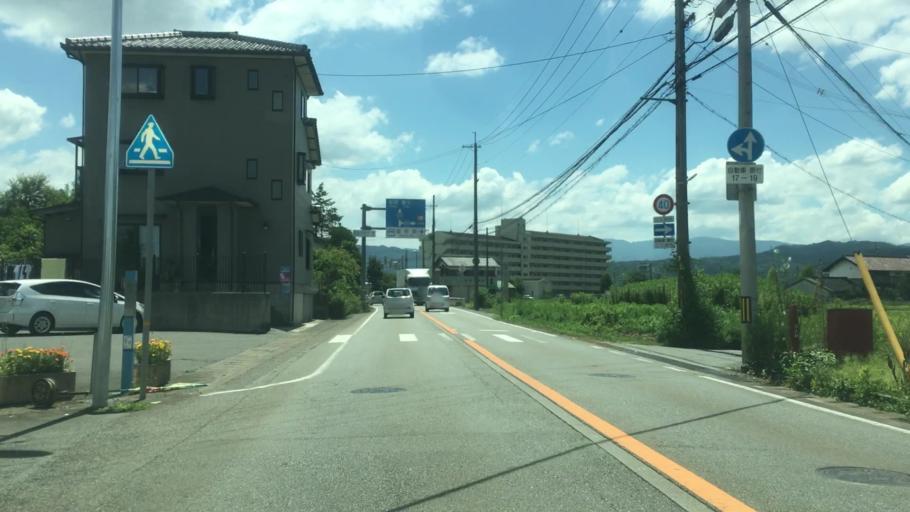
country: JP
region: Hyogo
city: Toyooka
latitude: 35.4969
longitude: 134.8029
